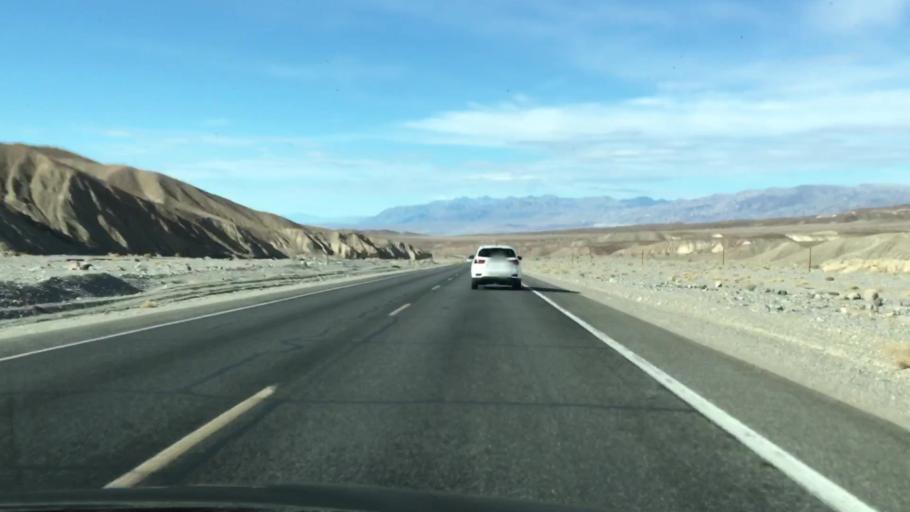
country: US
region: Nevada
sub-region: Nye County
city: Beatty
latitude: 36.4273
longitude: -116.8131
